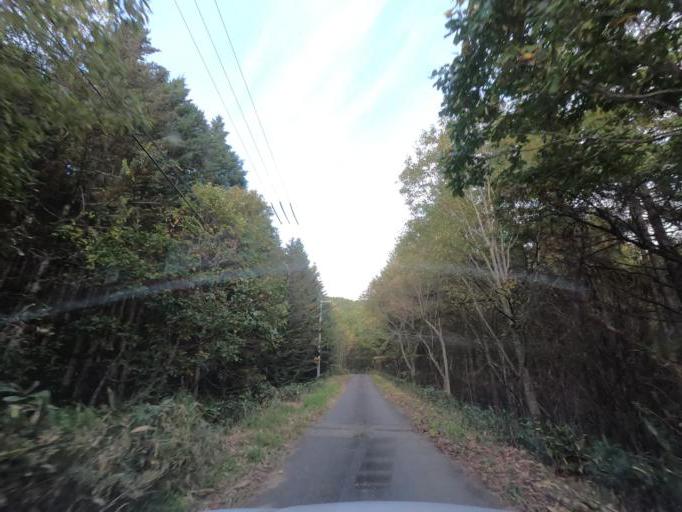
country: JP
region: Hokkaido
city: Obihiro
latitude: 42.5880
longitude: 143.3106
